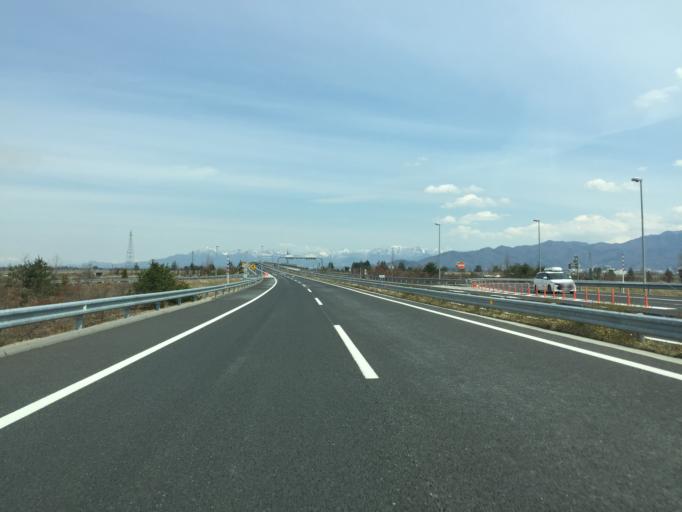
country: JP
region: Yamagata
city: Tendo
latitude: 38.3055
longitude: 140.3132
